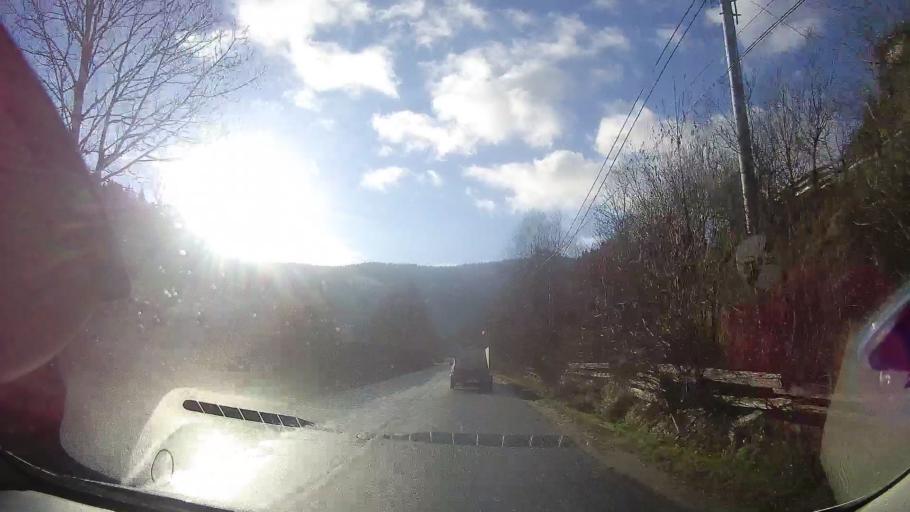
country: RO
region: Alba
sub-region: Comuna Vadu Motilor
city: Vadu Motilor
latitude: 46.4024
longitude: 22.9628
